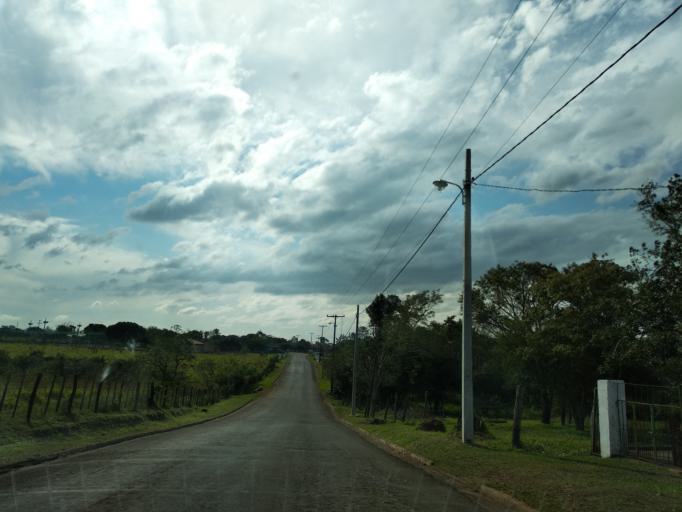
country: PY
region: Itapua
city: San Juan del Parana
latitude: -27.3052
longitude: -55.9664
